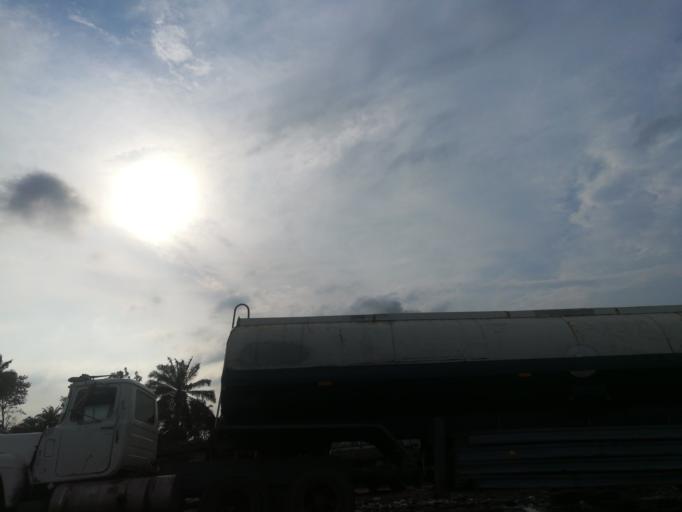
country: NG
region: Rivers
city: Okrika
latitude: 4.7719
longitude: 7.1050
